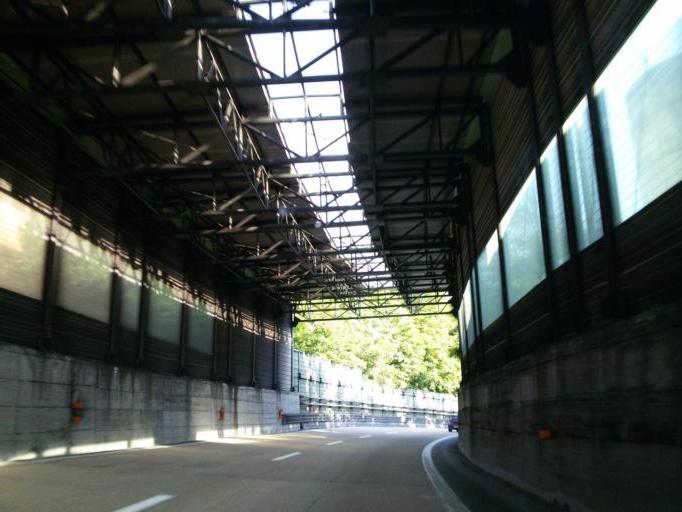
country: IT
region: Liguria
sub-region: Provincia di Genova
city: Manesseno
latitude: 44.4616
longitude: 8.9024
